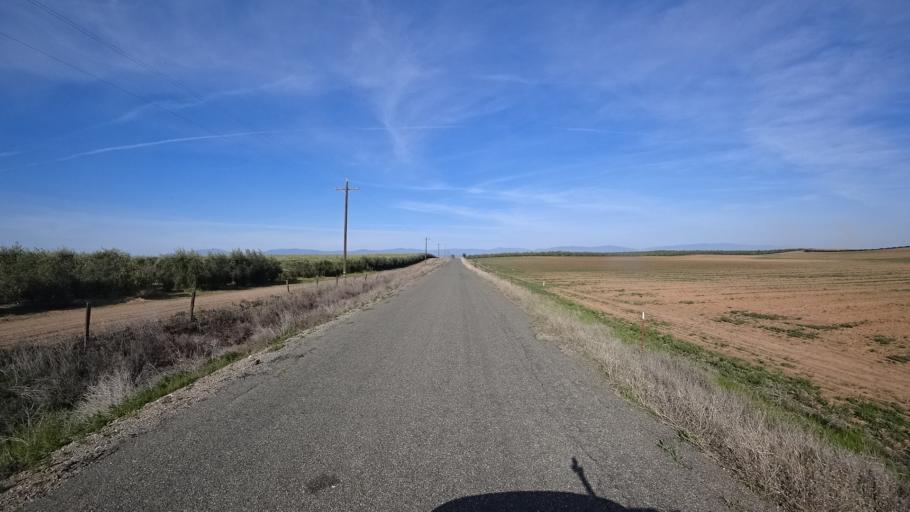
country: US
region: California
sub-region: Glenn County
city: Orland
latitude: 39.6686
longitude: -122.2750
